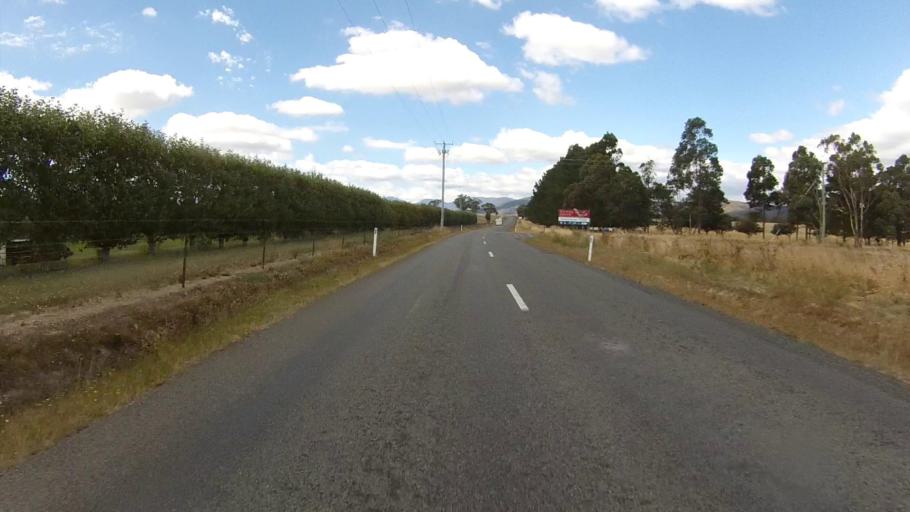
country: AU
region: Tasmania
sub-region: Derwent Valley
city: New Norfolk
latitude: -42.7492
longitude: 146.9738
